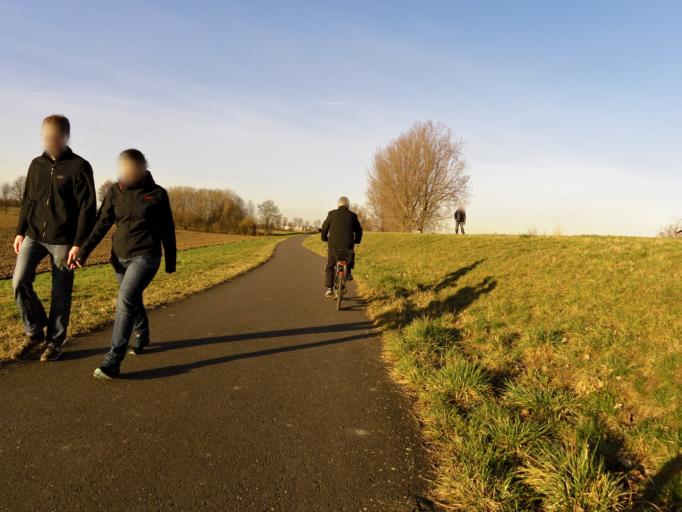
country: DE
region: Rheinland-Pfalz
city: Bobenheim-Roxheim
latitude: 49.5590
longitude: 8.4117
